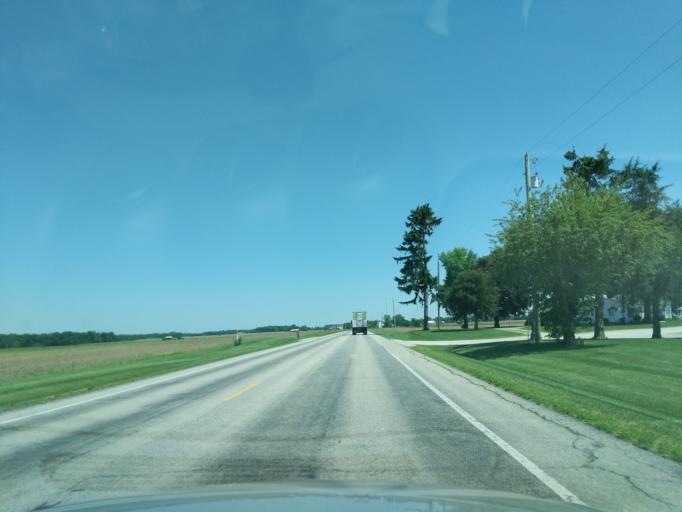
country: US
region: Indiana
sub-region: Huntington County
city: Roanoke
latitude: 40.9862
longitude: -85.4716
